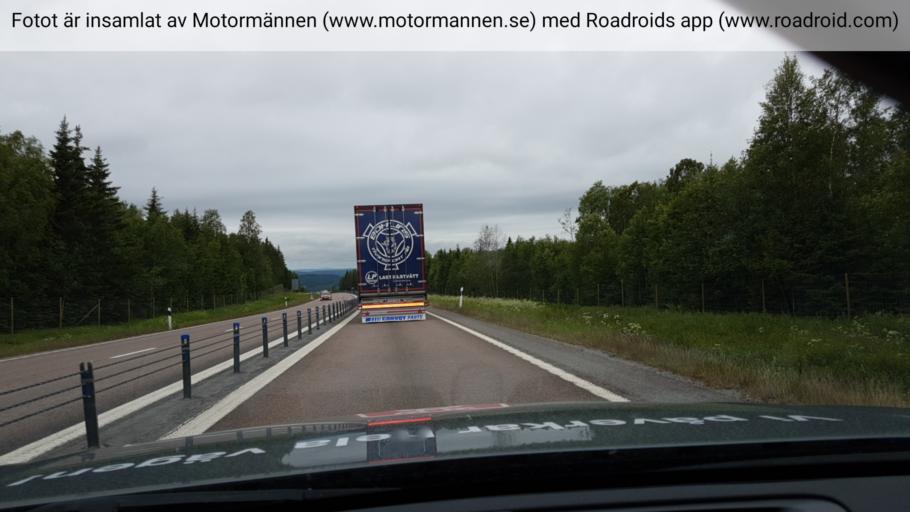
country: SE
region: Vaesternorrland
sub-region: Timra Kommun
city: Soraker
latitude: 62.5339
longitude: 17.5094
